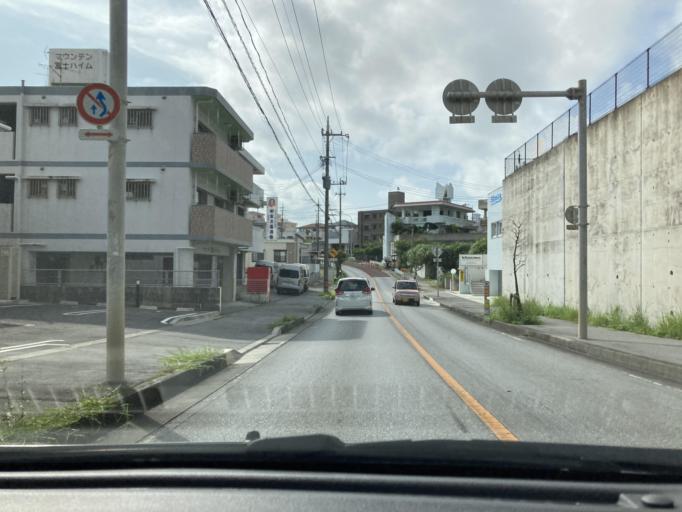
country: JP
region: Okinawa
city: Ginowan
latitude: 26.2574
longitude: 127.7688
